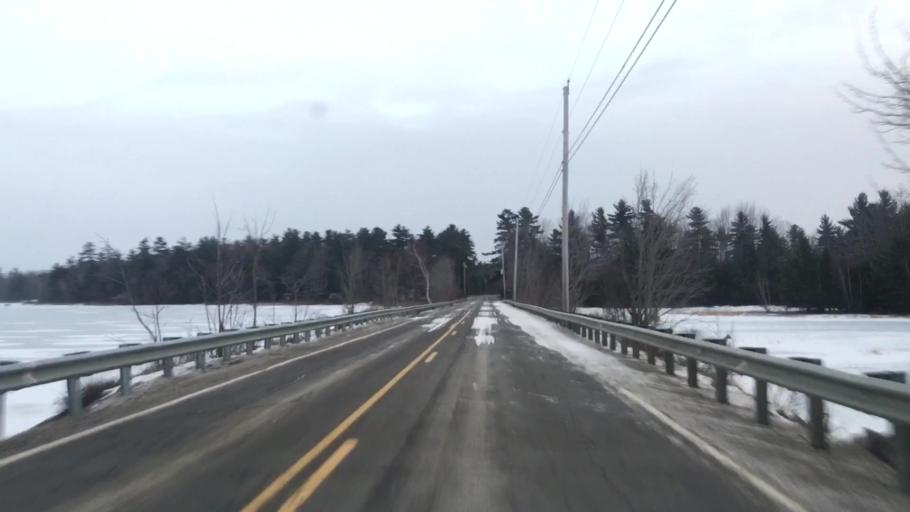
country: US
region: Maine
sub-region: Hancock County
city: Ellsworth
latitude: 44.6140
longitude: -68.3868
